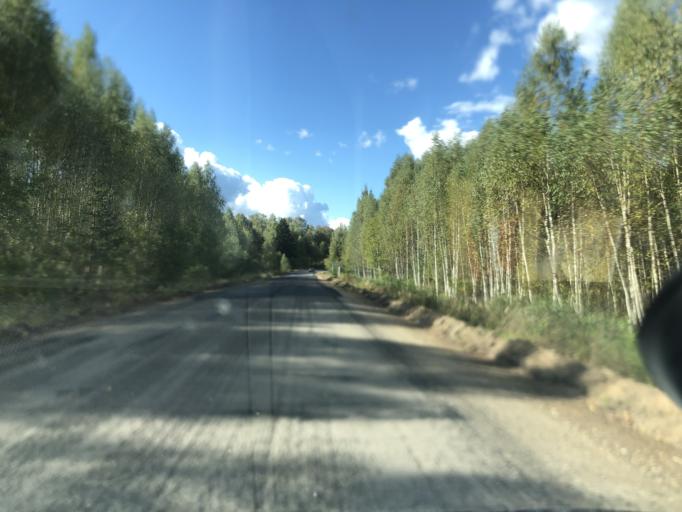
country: RU
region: Jaroslavl
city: Porech'ye-Rybnoye
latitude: 56.9679
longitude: 39.4320
